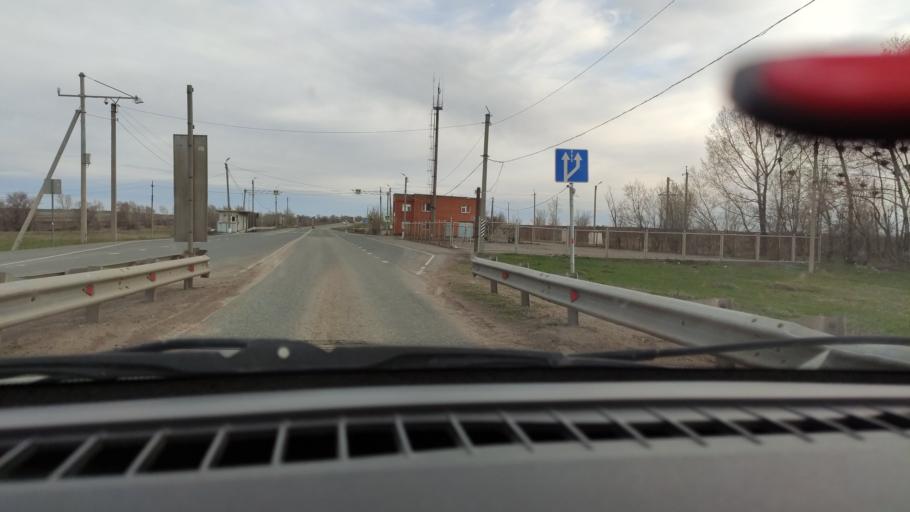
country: RU
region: Orenburg
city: Sakmara
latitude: 52.1709
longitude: 55.2910
